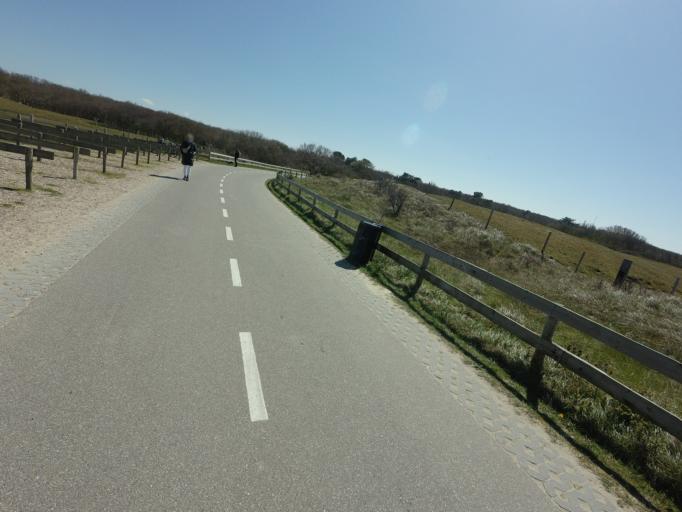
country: NL
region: Zeeland
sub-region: Gemeente Middelburg
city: Middelburg
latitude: 51.5813
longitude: 3.5434
